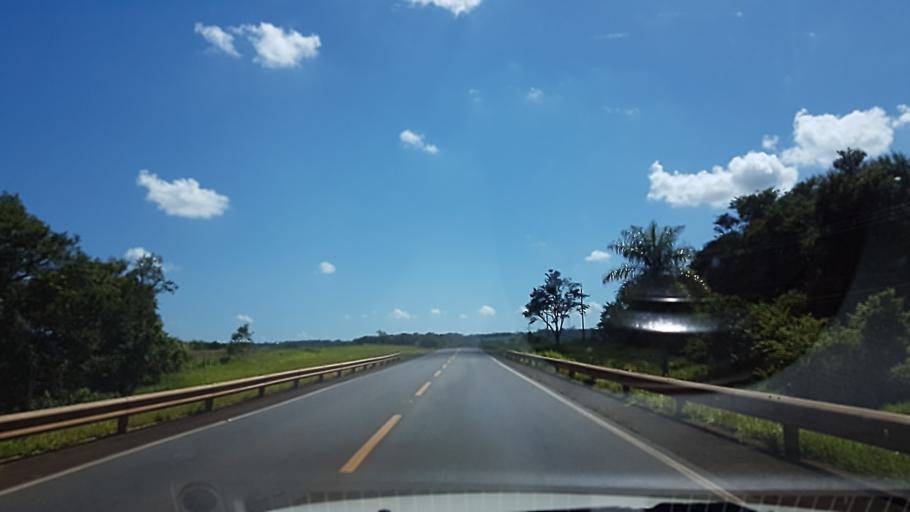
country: PY
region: Itapua
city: Carmen del Parana
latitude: -27.2150
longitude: -56.0908
